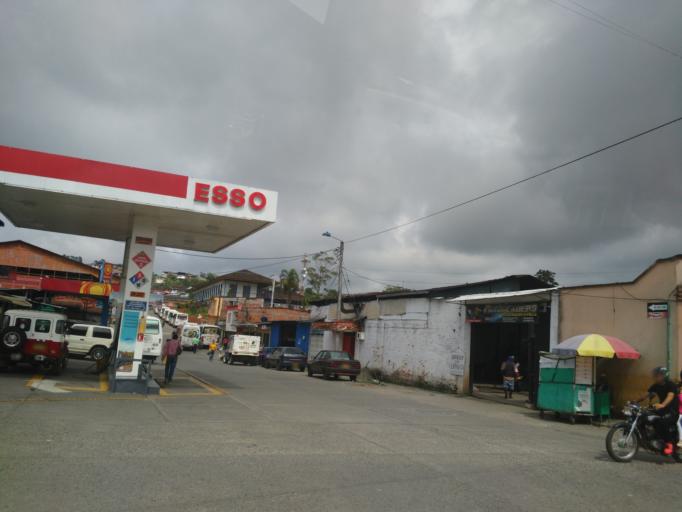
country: CO
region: Valle del Cauca
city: Sevilla
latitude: 4.2665
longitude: -75.9330
